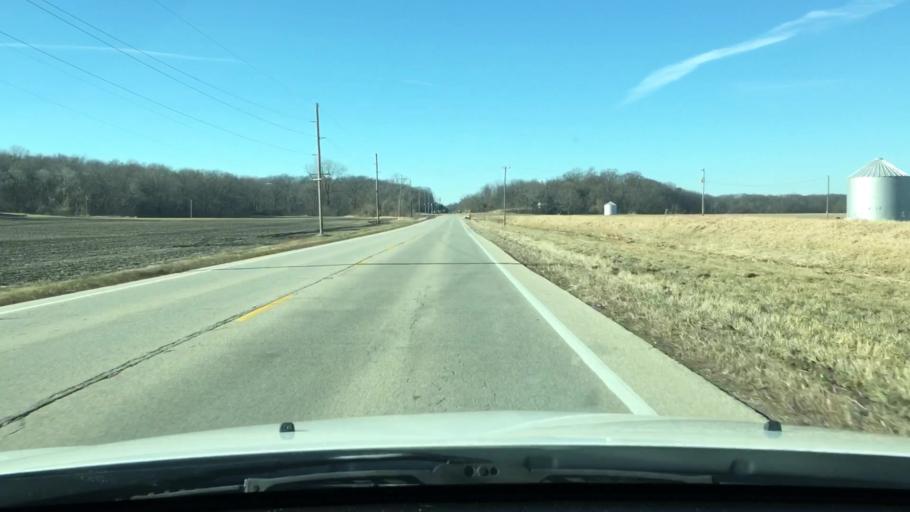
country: US
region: Illinois
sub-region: Mason County
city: Havana
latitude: 40.3041
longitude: -90.1324
